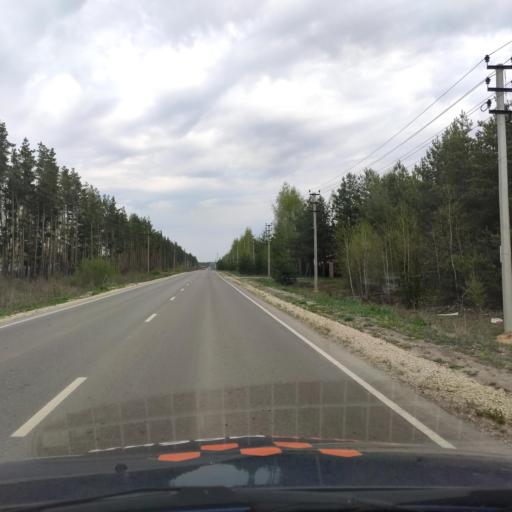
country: RU
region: Voronezj
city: Podgornoye
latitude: 51.8591
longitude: 39.1639
